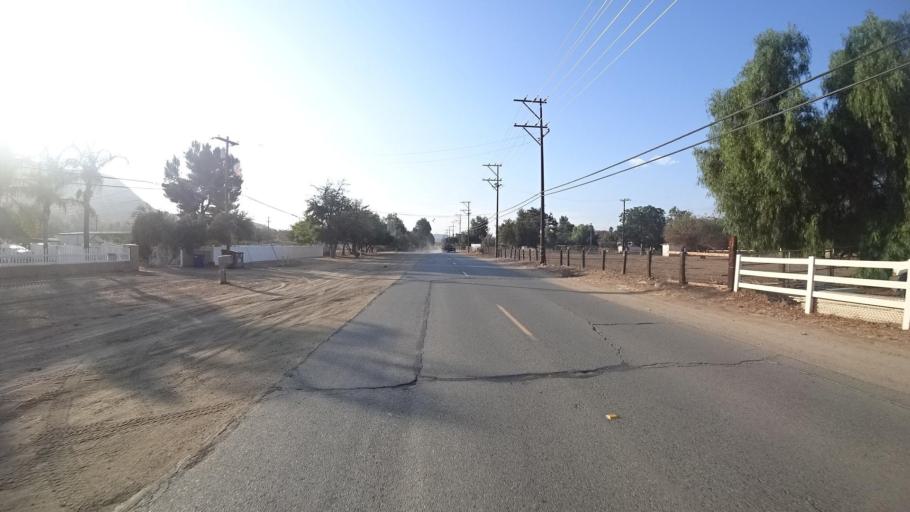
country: US
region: California
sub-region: San Diego County
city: Eucalyptus Hills
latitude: 32.8869
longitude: -116.9252
